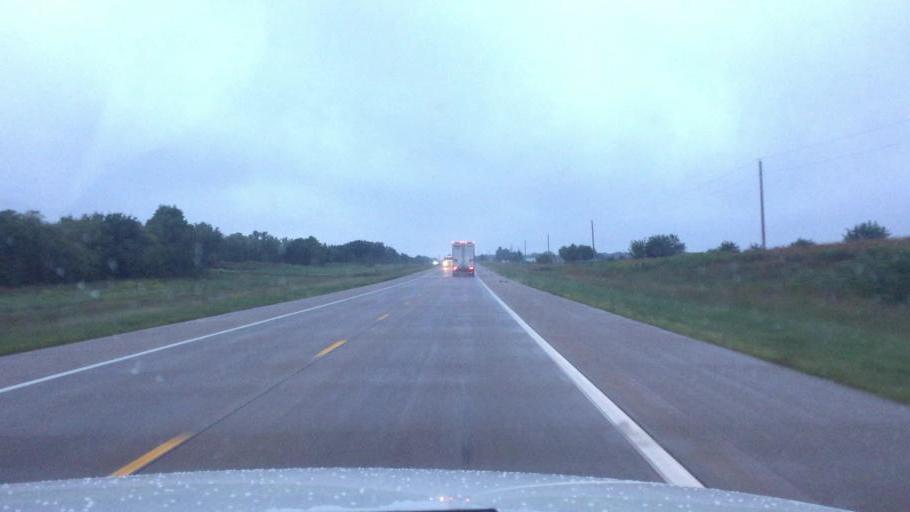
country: US
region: Kansas
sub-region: Neosho County
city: Chanute
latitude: 37.5086
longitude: -95.4709
